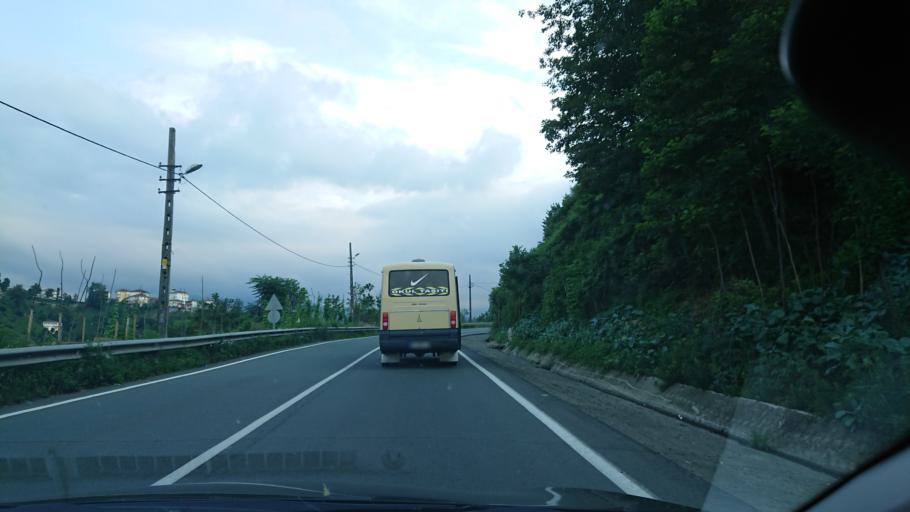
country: TR
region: Rize
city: Cayeli
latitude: 41.0788
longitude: 40.7134
